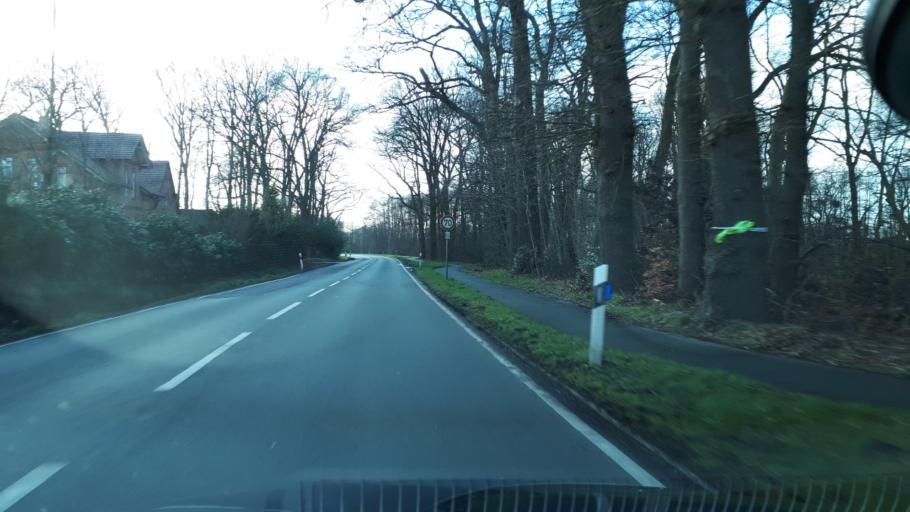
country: DE
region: Lower Saxony
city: Molbergen
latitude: 52.8507
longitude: 7.9862
